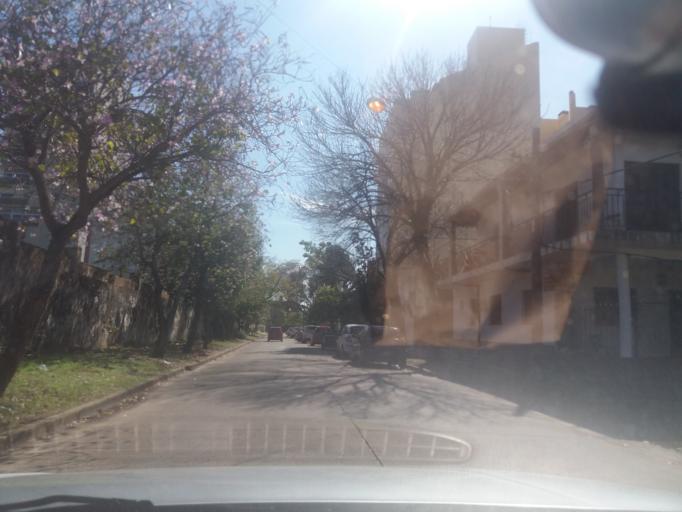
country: AR
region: Corrientes
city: Corrientes
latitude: -27.4721
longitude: -58.8511
